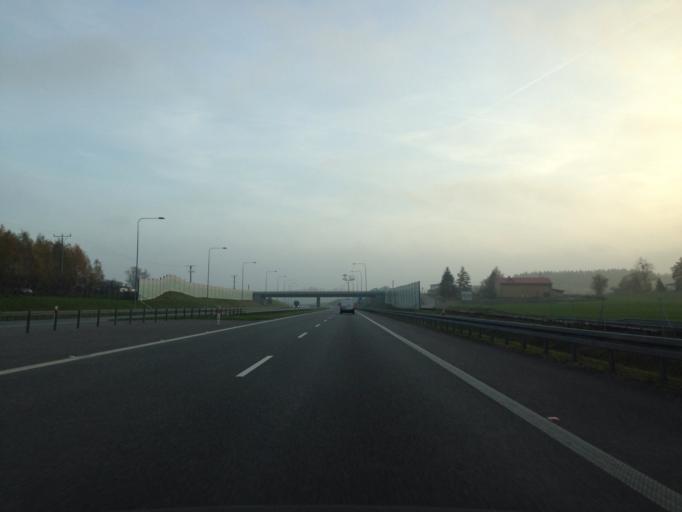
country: PL
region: Warmian-Masurian Voivodeship
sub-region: Powiat ostrodzki
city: Maldyty
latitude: 53.8895
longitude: 19.7335
